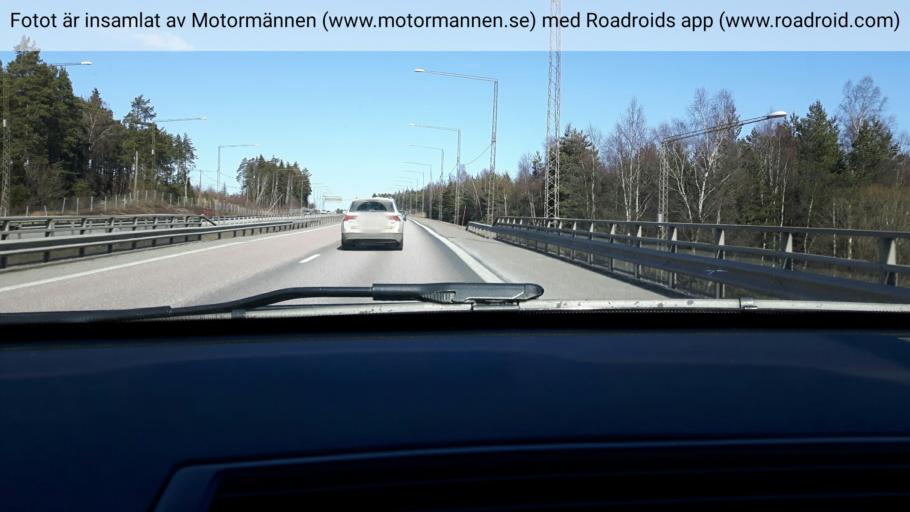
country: SE
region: Stockholm
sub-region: Sigtuna Kommun
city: Rosersberg
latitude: 59.6189
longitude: 17.9009
